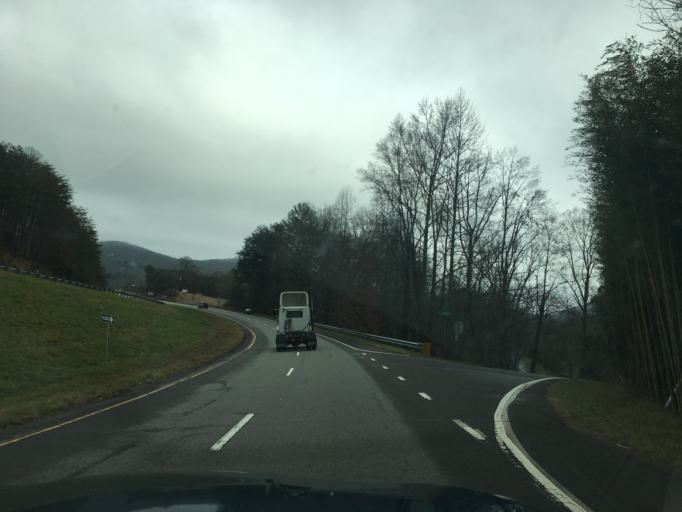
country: US
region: Georgia
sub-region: Fannin County
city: McCaysville
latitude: 35.0151
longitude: -84.3117
